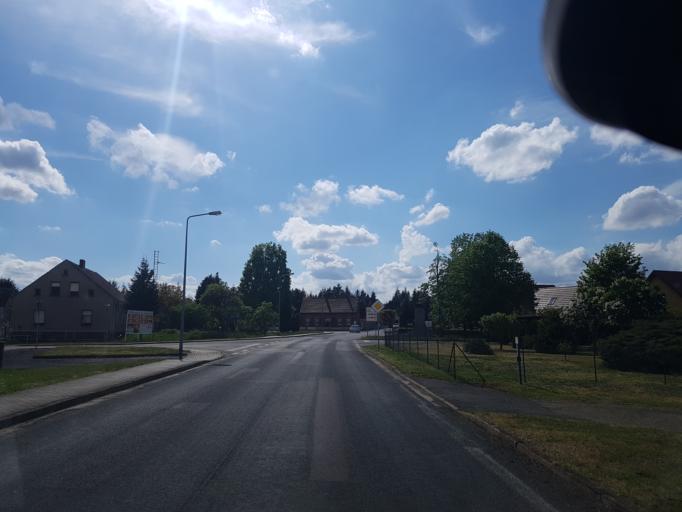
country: DE
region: Brandenburg
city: Spremberg
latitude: 51.6749
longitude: 14.4423
